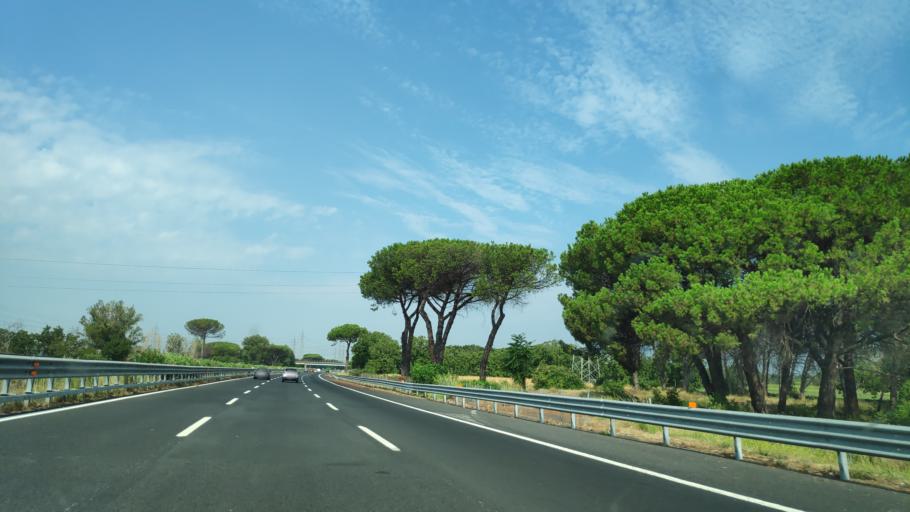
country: IT
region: Campania
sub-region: Provincia di Caserta
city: Maddaloni
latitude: 41.0119
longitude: 14.3848
